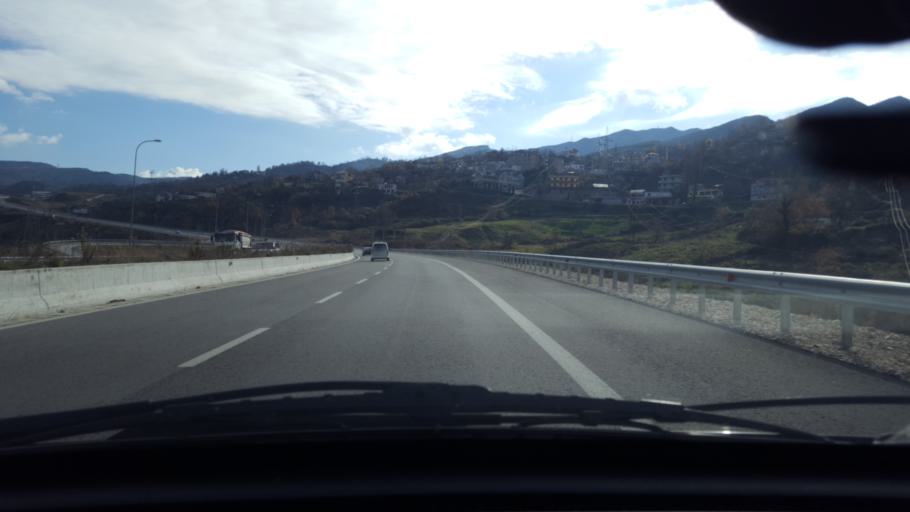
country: AL
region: Tirane
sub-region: Rrethi i Tiranes
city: Berzhite
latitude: 41.2298
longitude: 19.9297
